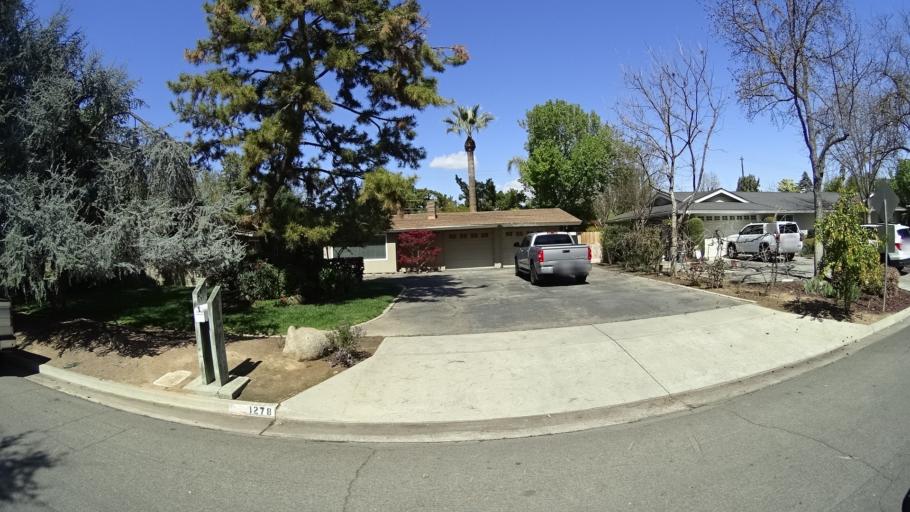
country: US
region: California
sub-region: Fresno County
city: Fresno
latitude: 36.8120
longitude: -119.8146
